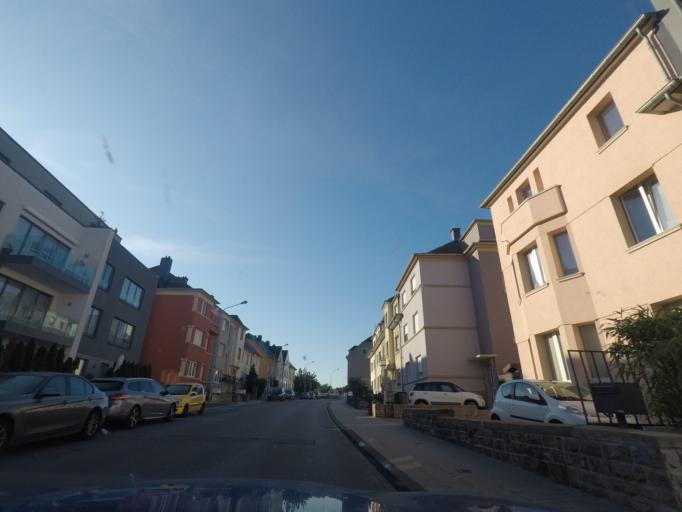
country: LU
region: Luxembourg
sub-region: Canton de Luxembourg
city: Luxembourg
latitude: 49.5928
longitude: 6.1413
